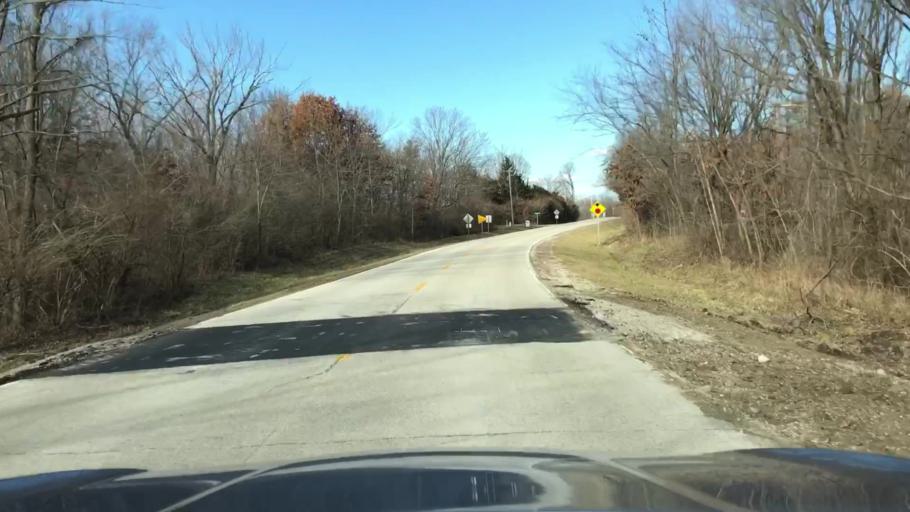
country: US
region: Illinois
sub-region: McLean County
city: Hudson
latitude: 40.6548
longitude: -88.9240
